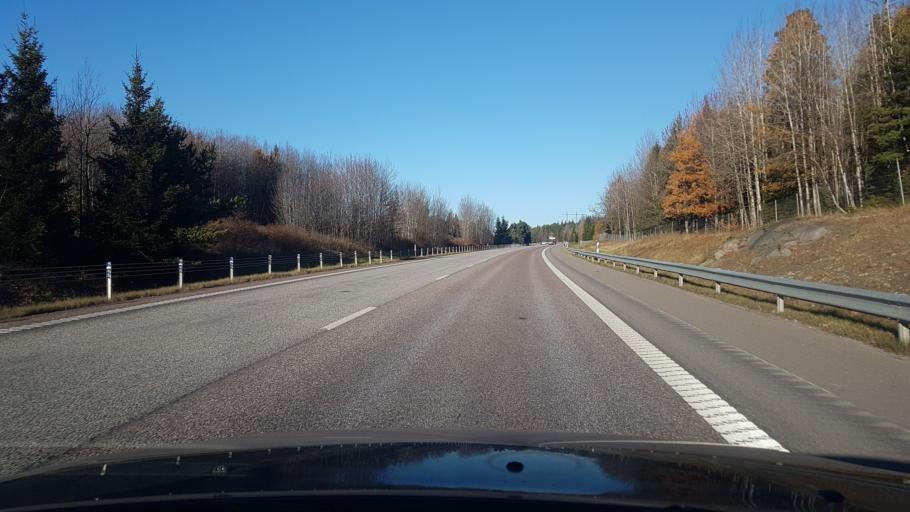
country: SE
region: Uppsala
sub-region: Uppsala Kommun
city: Alsike
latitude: 59.7808
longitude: 17.7800
